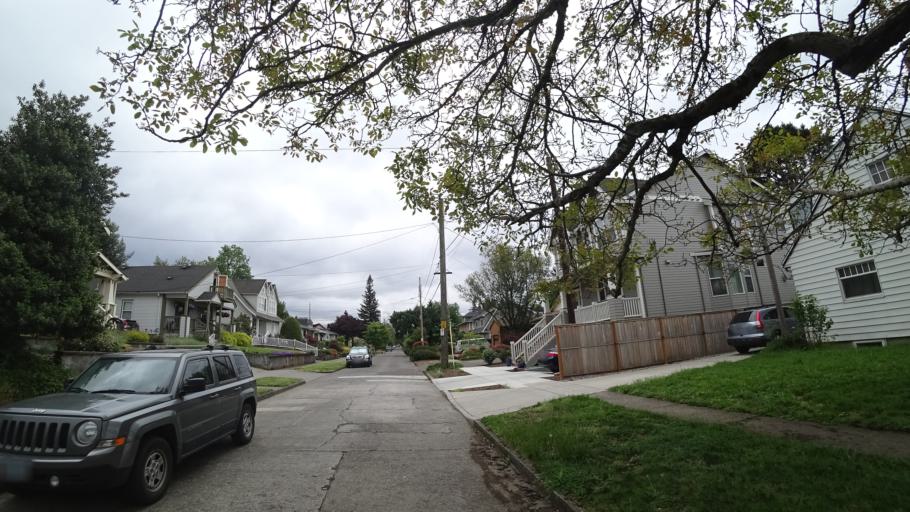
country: US
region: Oregon
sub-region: Clackamas County
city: Milwaukie
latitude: 45.4919
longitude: -122.6178
